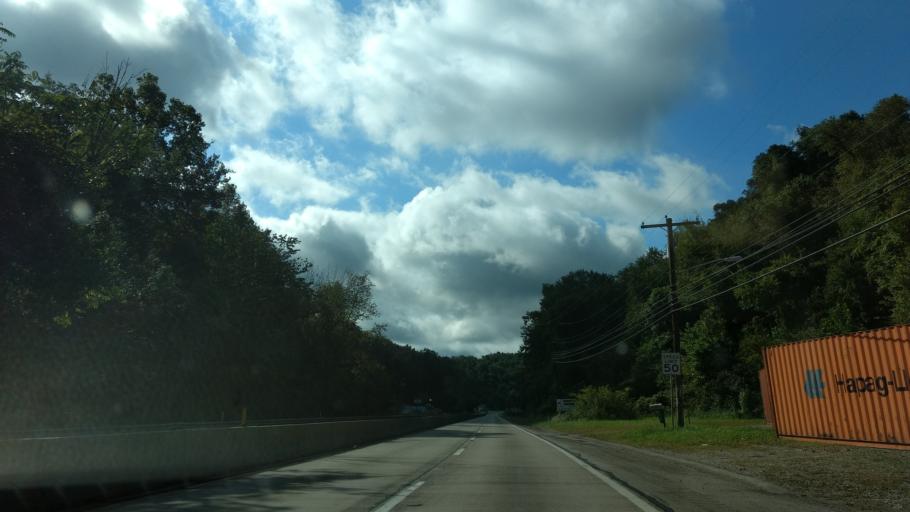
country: US
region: Pennsylvania
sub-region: Allegheny County
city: Elizabeth
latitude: 40.2551
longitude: -79.8791
